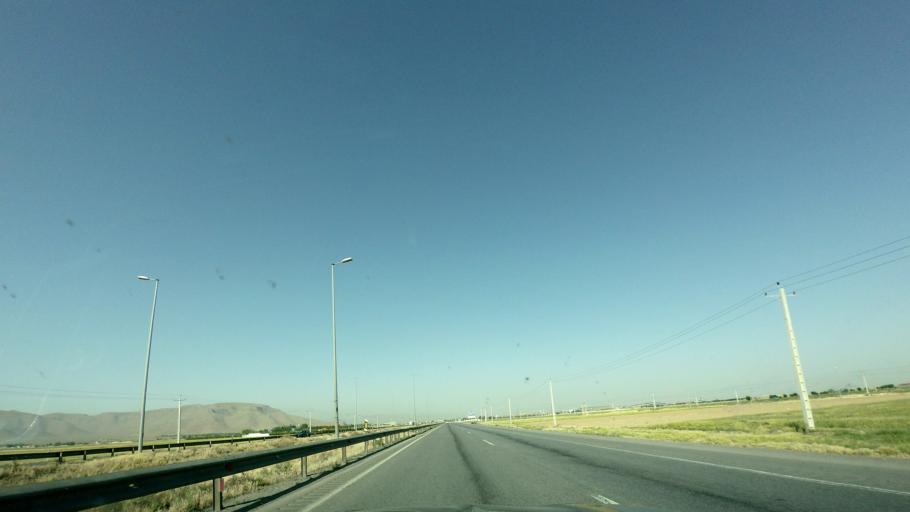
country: IR
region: Markazi
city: Arak
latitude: 34.1580
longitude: 50.0082
